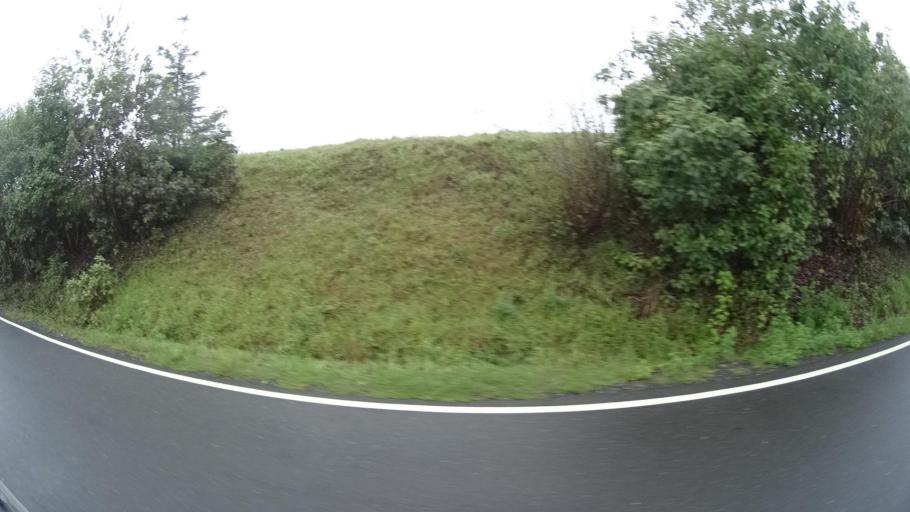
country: US
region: California
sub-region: Humboldt County
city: Westhaven-Moonstone
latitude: 41.1690
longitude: -123.9179
